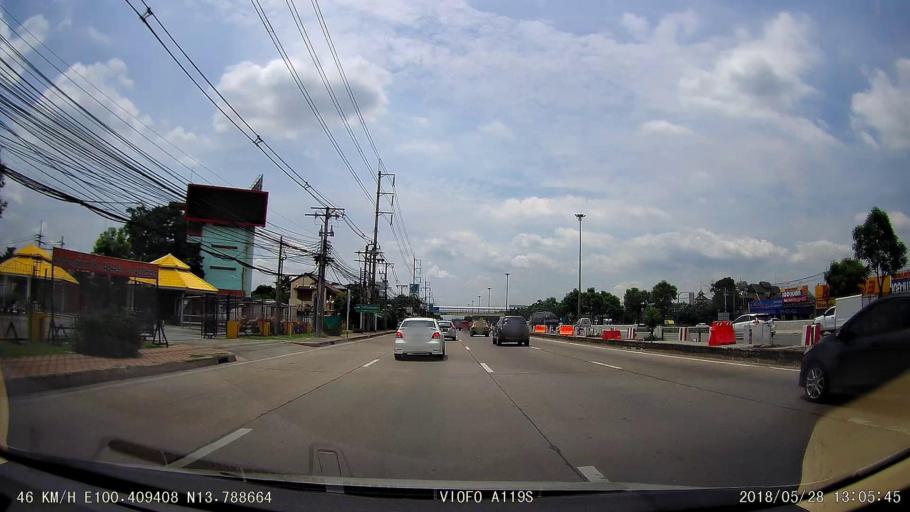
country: TH
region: Bangkok
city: Taling Chan
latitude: 13.7889
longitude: 100.4094
